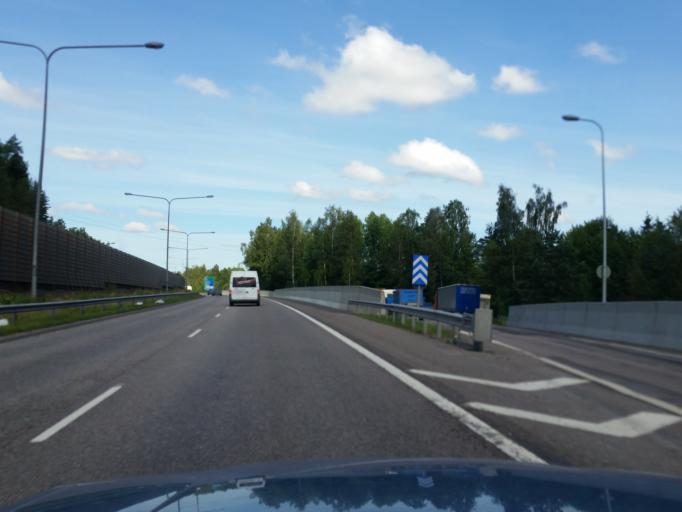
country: FI
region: Uusimaa
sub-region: Helsinki
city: Espoo
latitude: 60.2384
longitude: 24.5795
